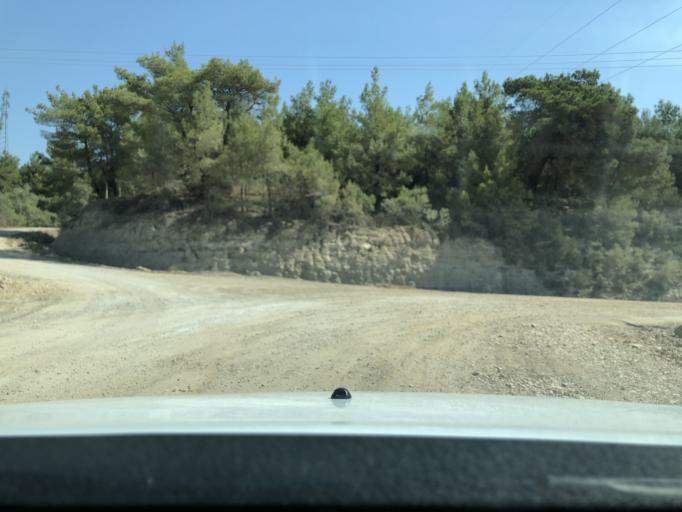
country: TR
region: Antalya
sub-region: Manavgat
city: Manavgat
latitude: 36.8231
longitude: 31.4976
